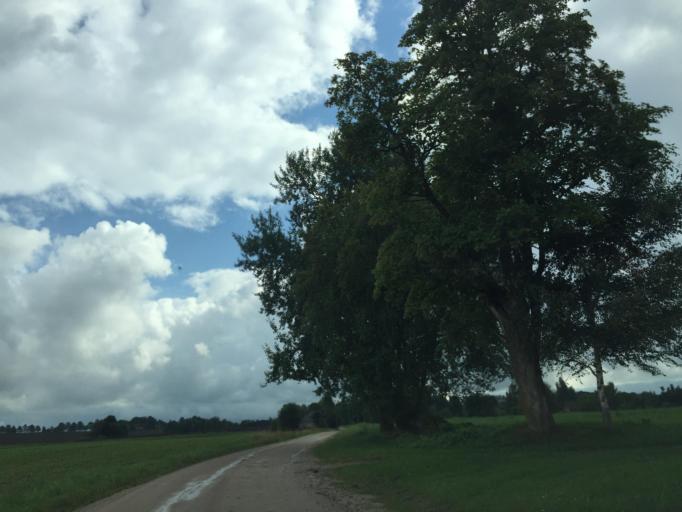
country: LV
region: Priekuli
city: Priekuli
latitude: 57.3398
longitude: 25.4844
